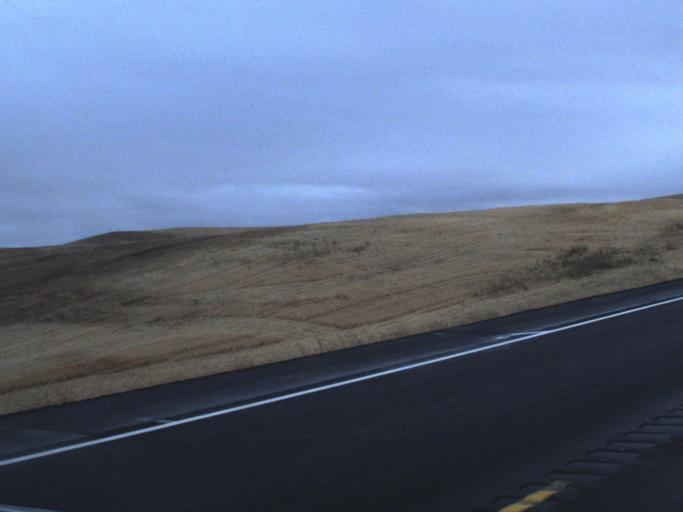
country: US
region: Washington
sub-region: Spokane County
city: Cheney
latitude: 47.3607
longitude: -117.3807
